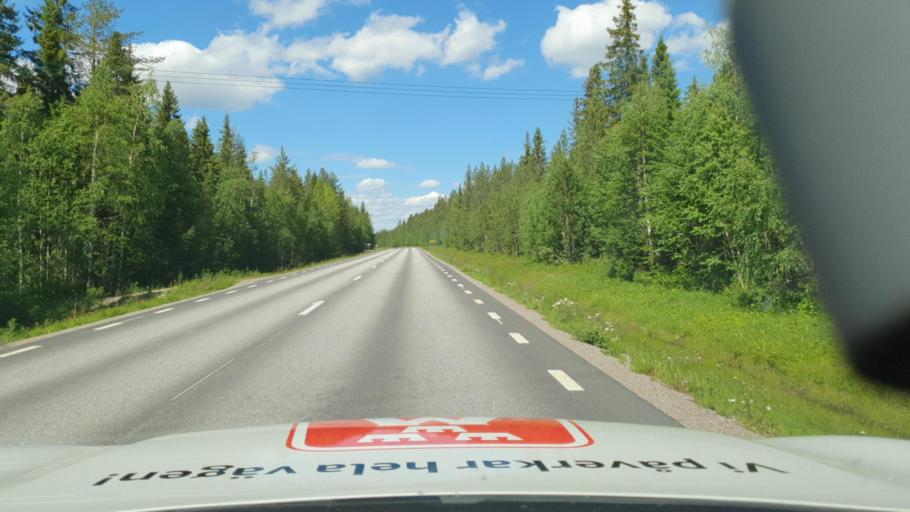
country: SE
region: Vaesterbotten
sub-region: Skelleftea Kommun
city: Boliden
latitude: 64.9120
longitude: 20.3420
